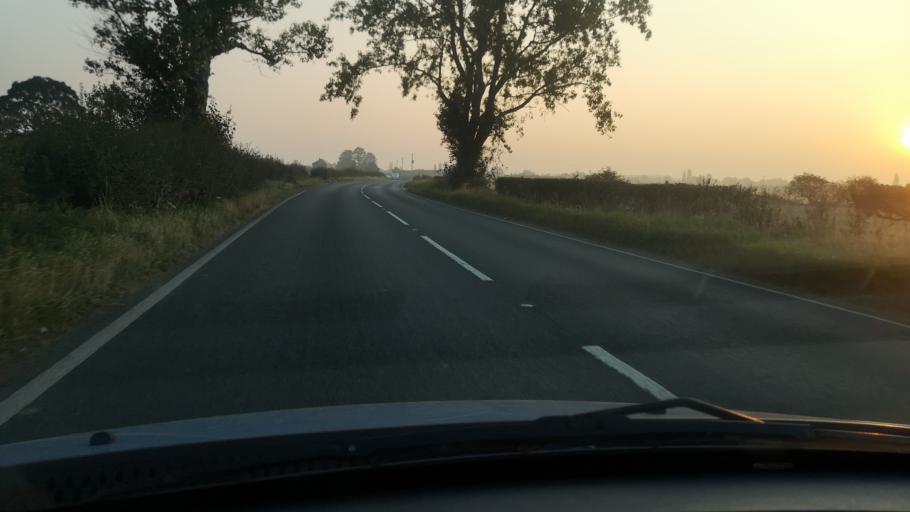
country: GB
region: England
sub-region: Doncaster
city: Stainforth
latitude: 53.5929
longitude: -1.0473
